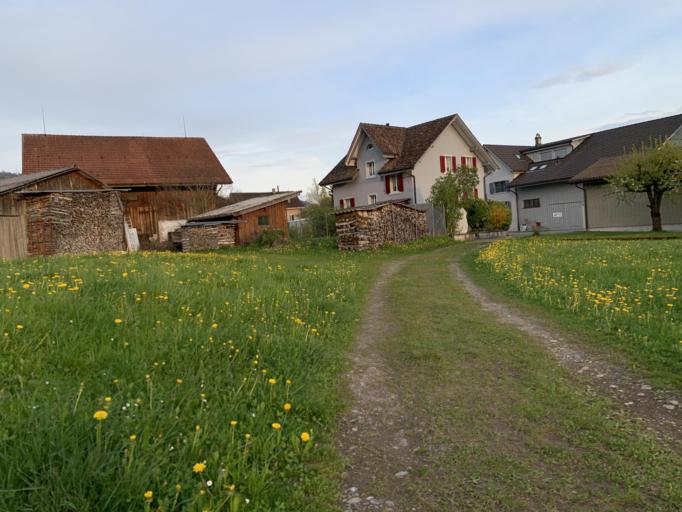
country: CH
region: Zurich
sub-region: Bezirk Hinwil
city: Hinwil
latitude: 47.2894
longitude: 8.8397
